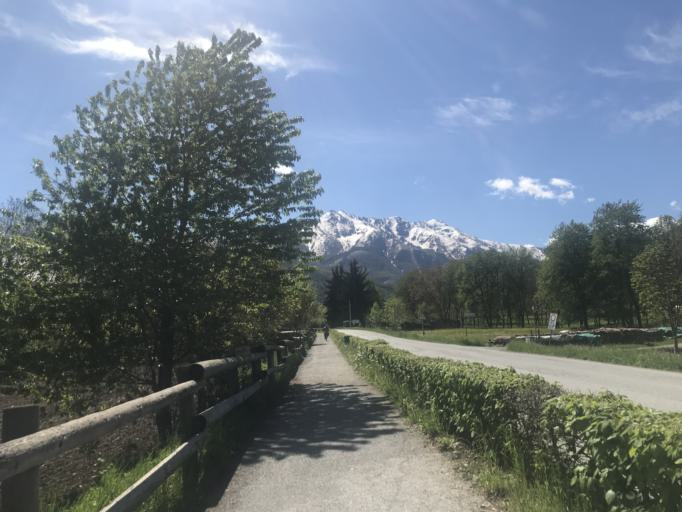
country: IT
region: Piedmont
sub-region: Provincia di Cuneo
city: Boves
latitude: 44.3234
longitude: 7.5626
